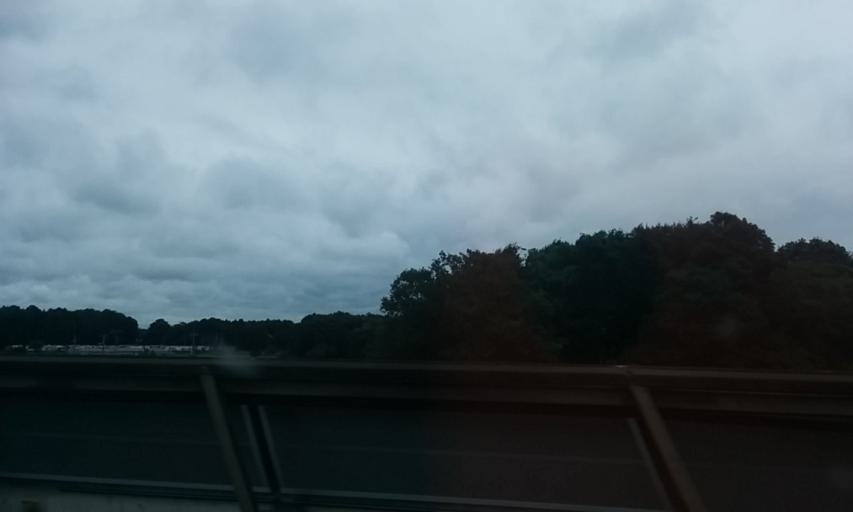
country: JP
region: Ibaraki
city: Koga
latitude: 36.2200
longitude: 139.7550
